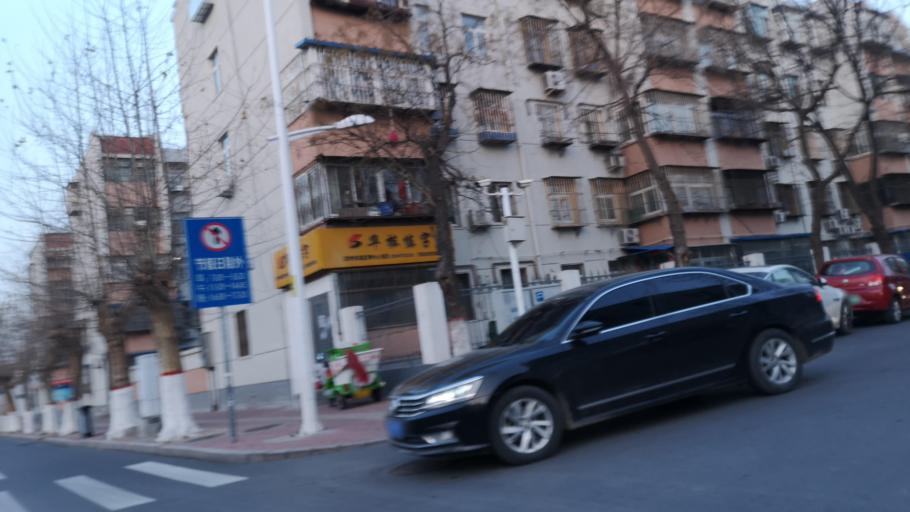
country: CN
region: Henan Sheng
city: Zhongyuanlu
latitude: 35.7769
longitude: 115.0795
